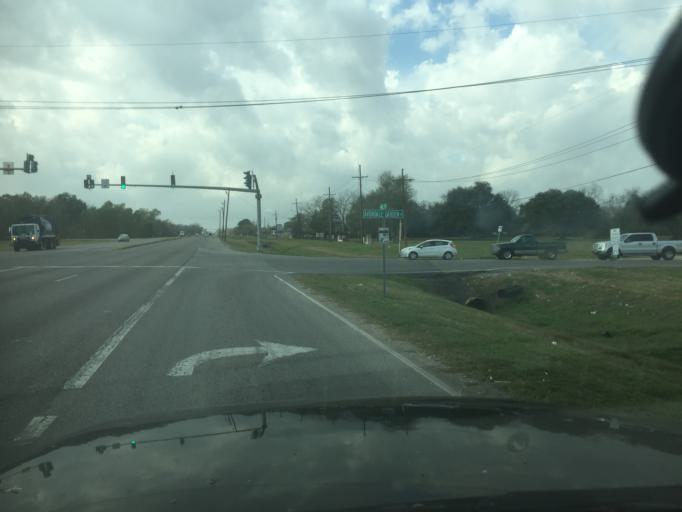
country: US
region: Louisiana
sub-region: Jefferson Parish
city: Avondale
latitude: 29.9105
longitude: -90.2109
